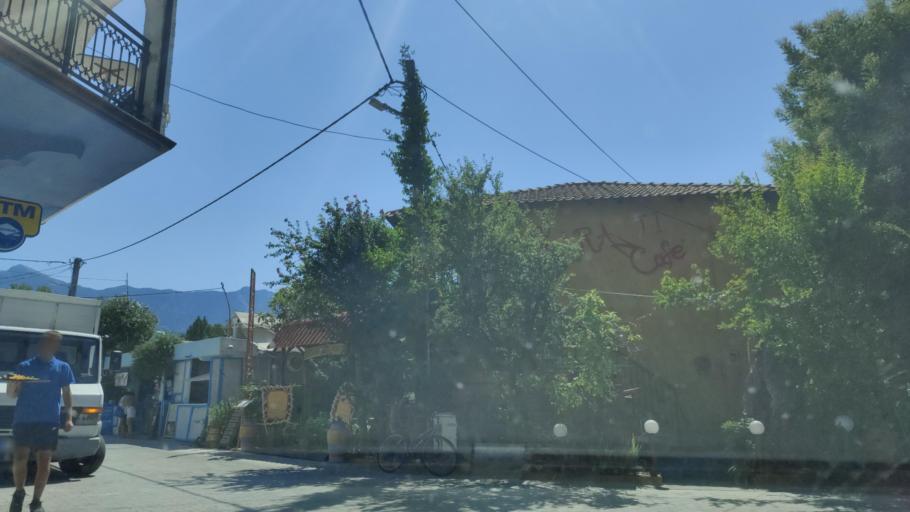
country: GR
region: East Macedonia and Thrace
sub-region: Nomos Kavalas
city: Thasos
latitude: 40.7820
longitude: 24.7138
